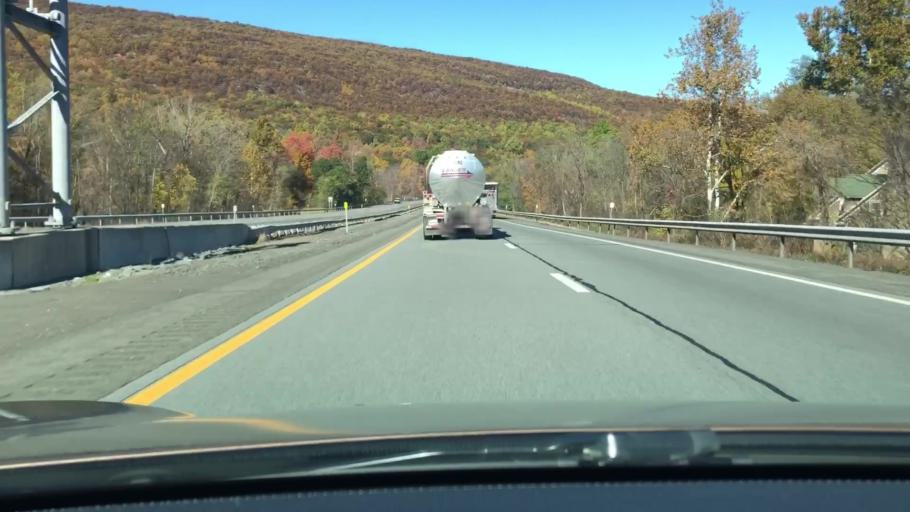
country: US
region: New York
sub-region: Orange County
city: Woodbury
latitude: 41.3730
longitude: -74.1020
